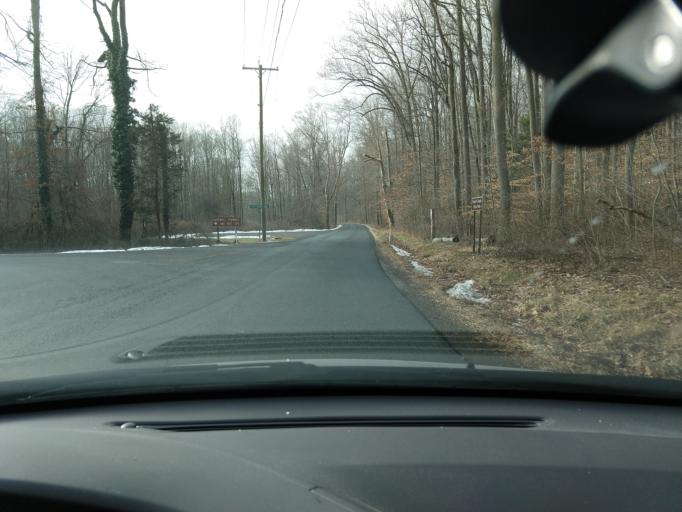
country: US
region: Pennsylvania
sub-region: Chester County
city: Elverson
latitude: 40.1963
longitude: -75.7966
